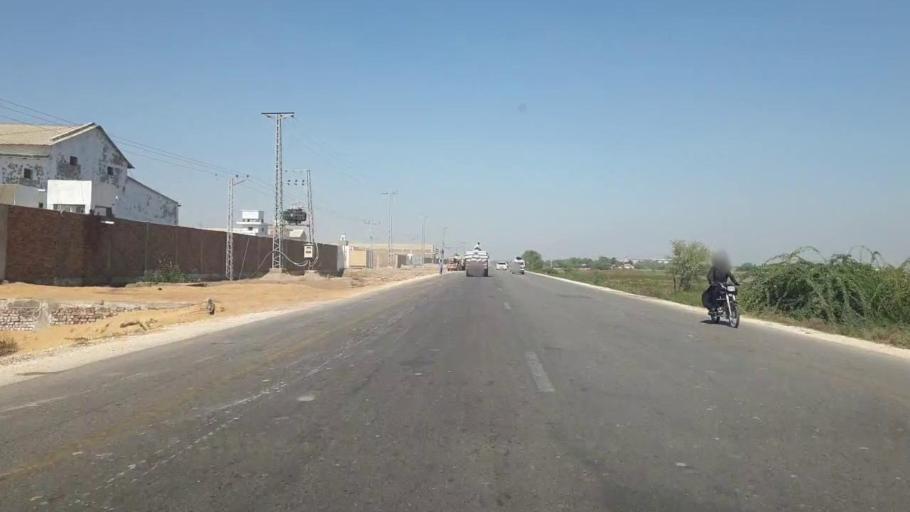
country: PK
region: Sindh
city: Talhar
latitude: 24.8654
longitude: 68.8167
